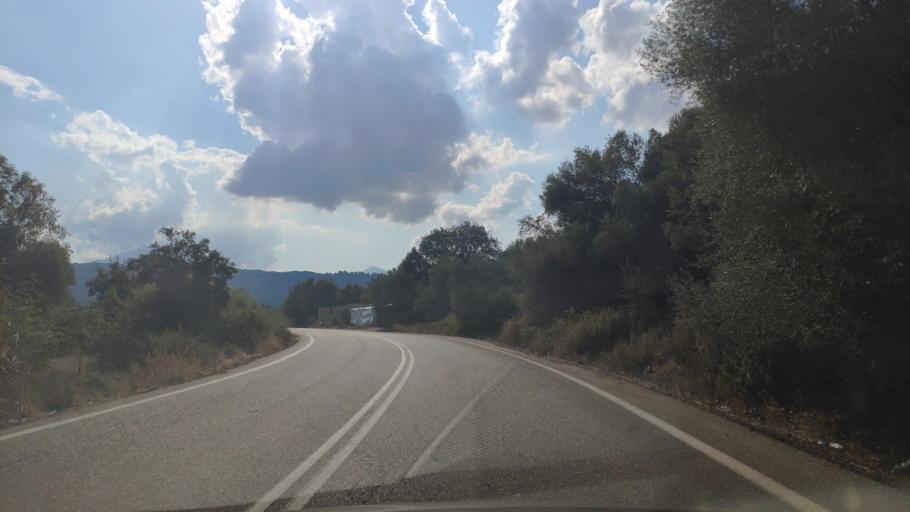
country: GR
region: West Greece
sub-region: Nomos Aitolias kai Akarnanias
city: Stanos
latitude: 38.7695
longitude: 21.1759
